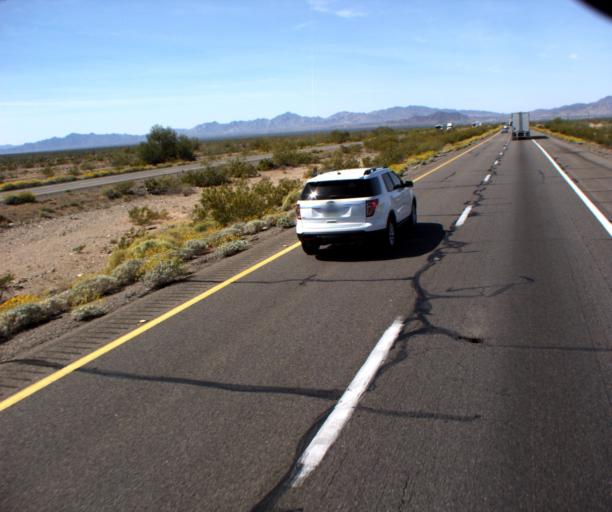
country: US
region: Arizona
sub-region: La Paz County
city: Quartzsite
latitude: 33.6780
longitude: -114.1132
